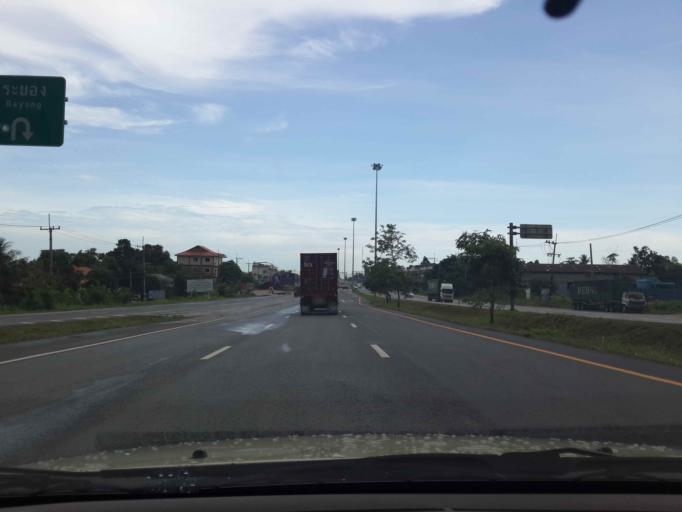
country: TH
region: Chon Buri
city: Phatthaya
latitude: 12.9546
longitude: 100.9868
